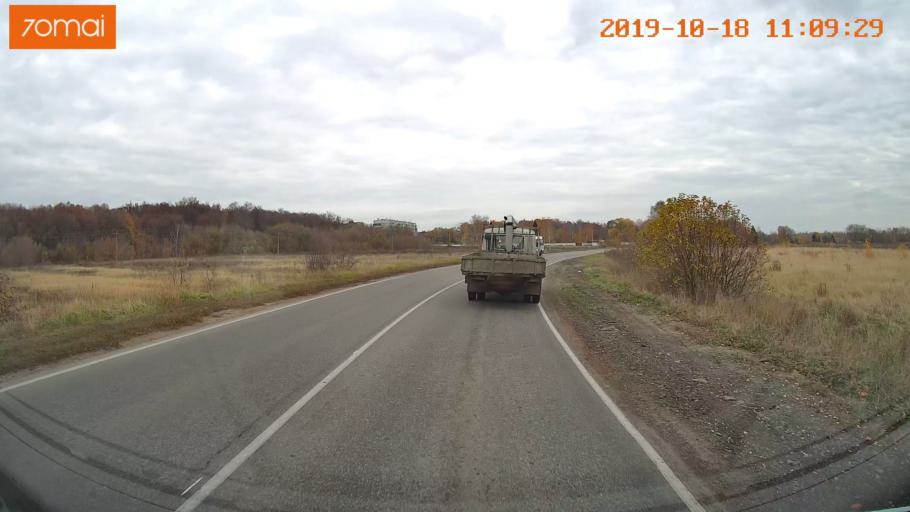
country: RU
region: Tula
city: Kimovsk
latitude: 53.9521
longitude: 38.5360
